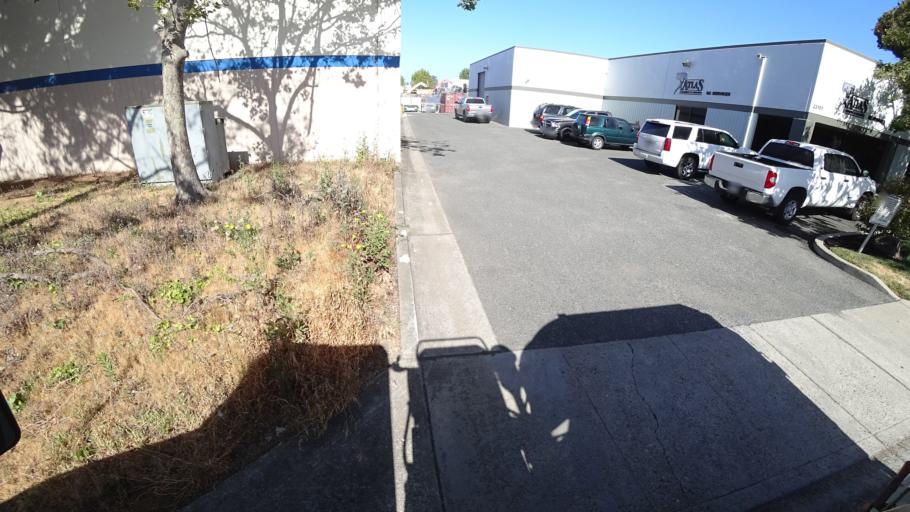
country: US
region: California
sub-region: Alameda County
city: San Lorenzo
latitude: 37.6435
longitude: -122.1315
